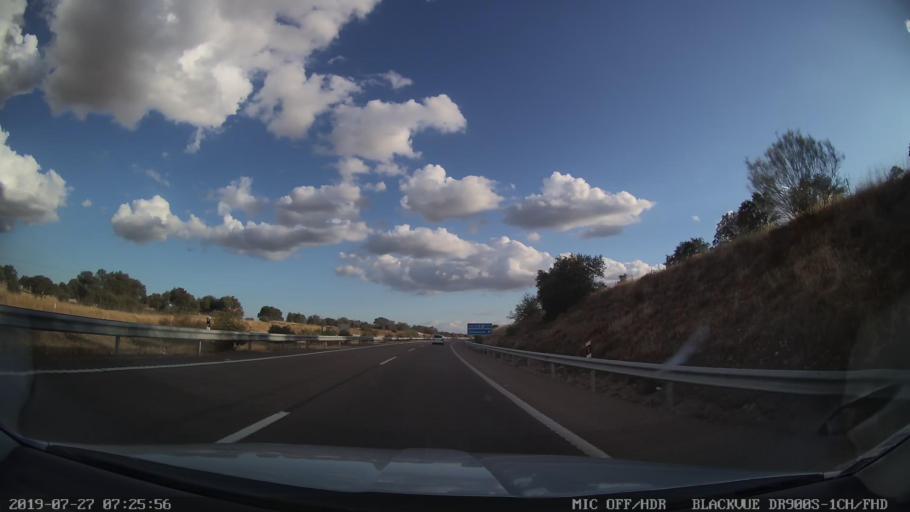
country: ES
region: Extremadura
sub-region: Provincia de Caceres
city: Villamesias
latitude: 39.2672
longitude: -5.8573
